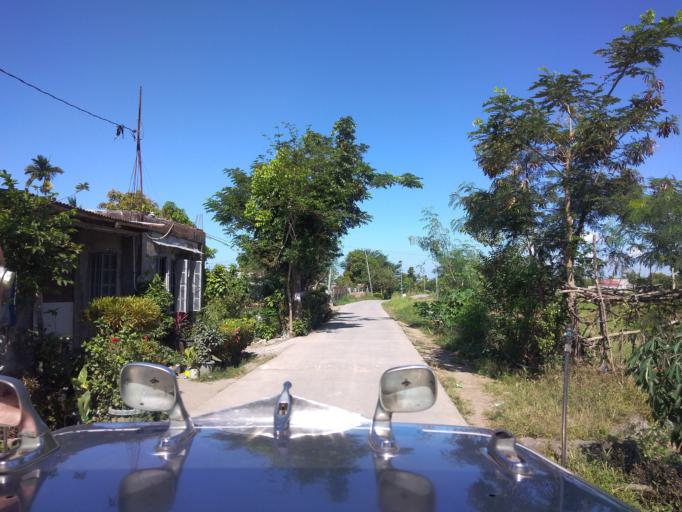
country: PH
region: Central Luzon
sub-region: Province of Pampanga
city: Salapungan
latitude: 15.1549
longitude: 120.9201
